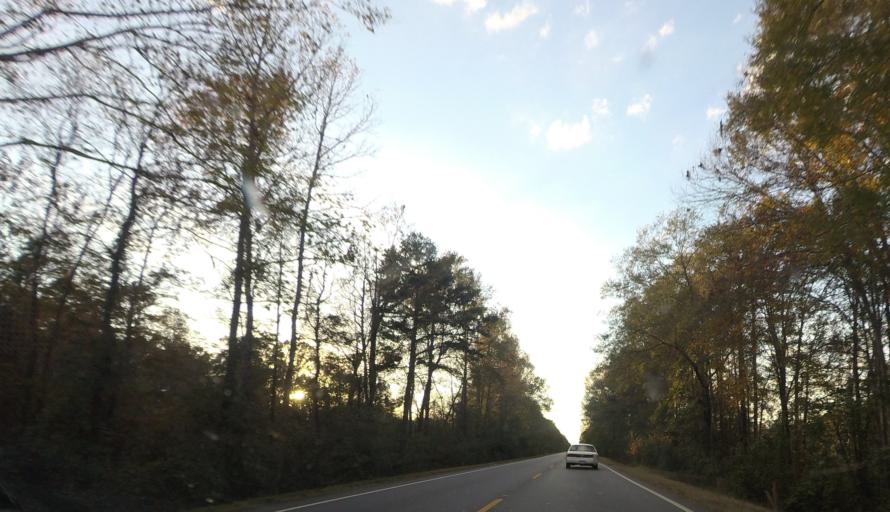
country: US
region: Georgia
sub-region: Houston County
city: Robins Air Force Base
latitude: 32.5421
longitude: -83.5162
